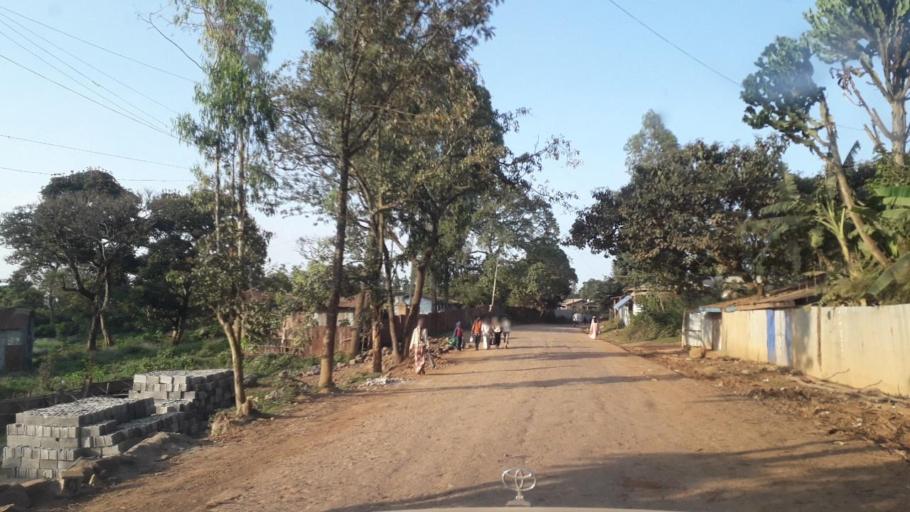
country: ET
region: Oromiya
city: Jima
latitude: 7.6362
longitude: 36.8362
